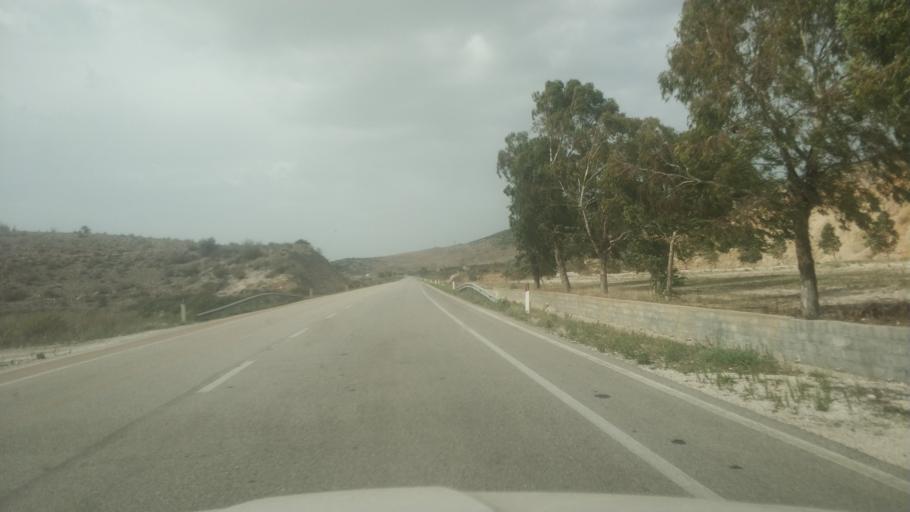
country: AL
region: Gjirokaster
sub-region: Rrethi i Tepelenes
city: Memaliaj
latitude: 40.3571
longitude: 19.9341
